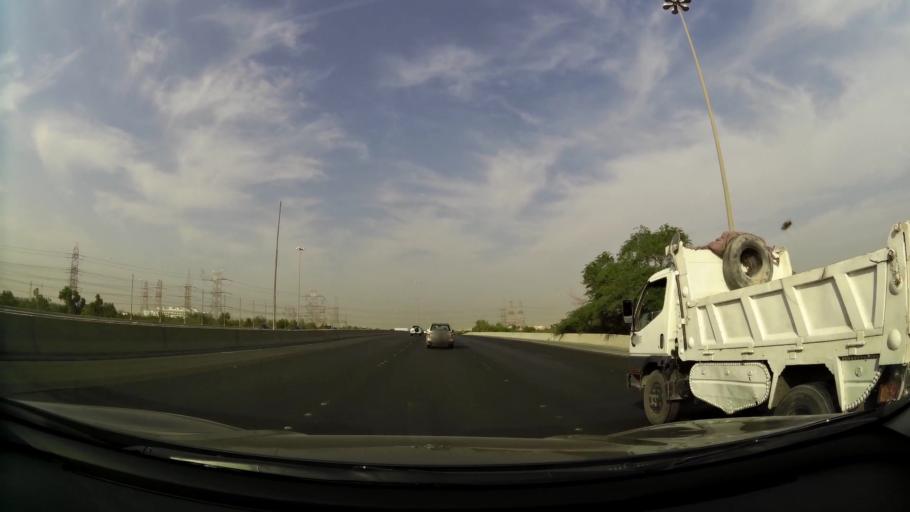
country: KW
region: Mubarak al Kabir
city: Sabah as Salim
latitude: 29.2648
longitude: 48.0430
